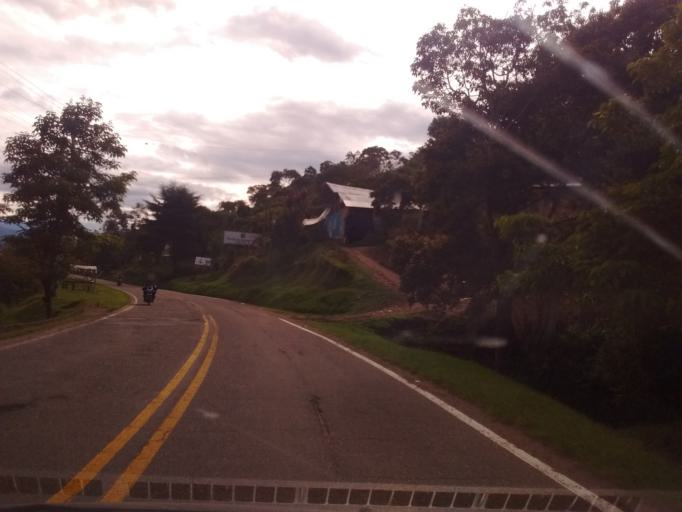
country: CO
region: Huila
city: San Agustin
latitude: 1.8764
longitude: -76.2574
